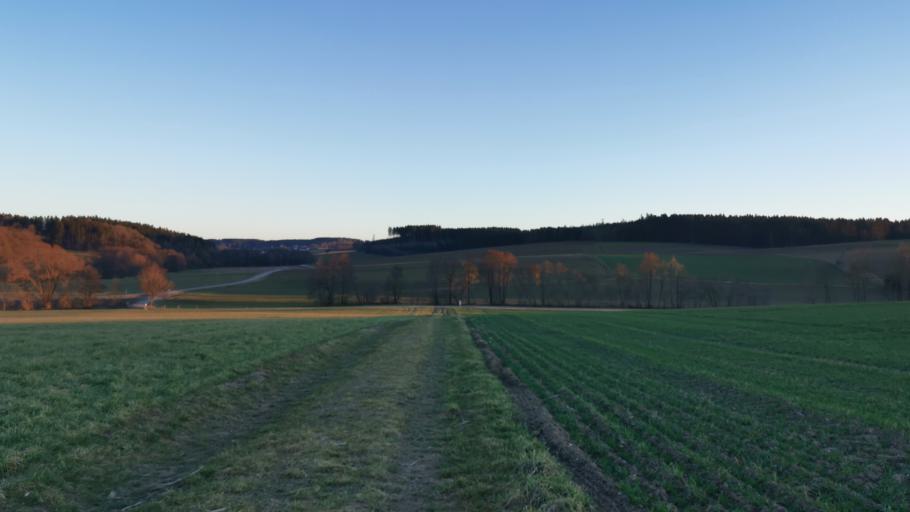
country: DE
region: Bavaria
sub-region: Lower Bavaria
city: Eching
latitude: 48.4915
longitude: 12.0609
